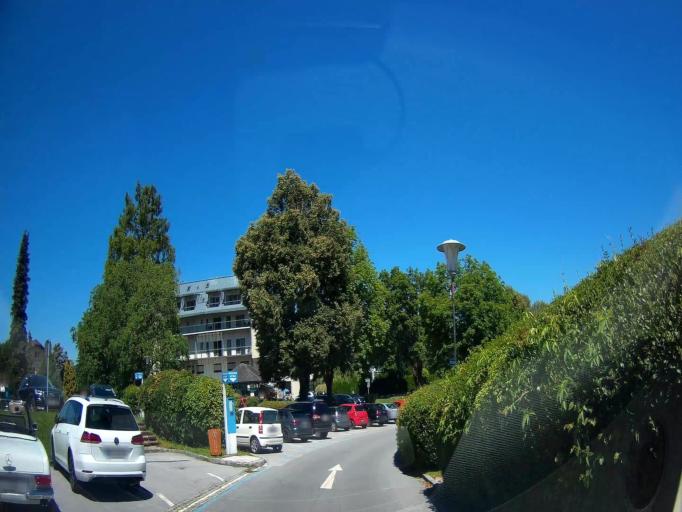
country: AT
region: Carinthia
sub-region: Politischer Bezirk Klagenfurt Land
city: Maria Worth
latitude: 46.6164
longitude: 14.1623
